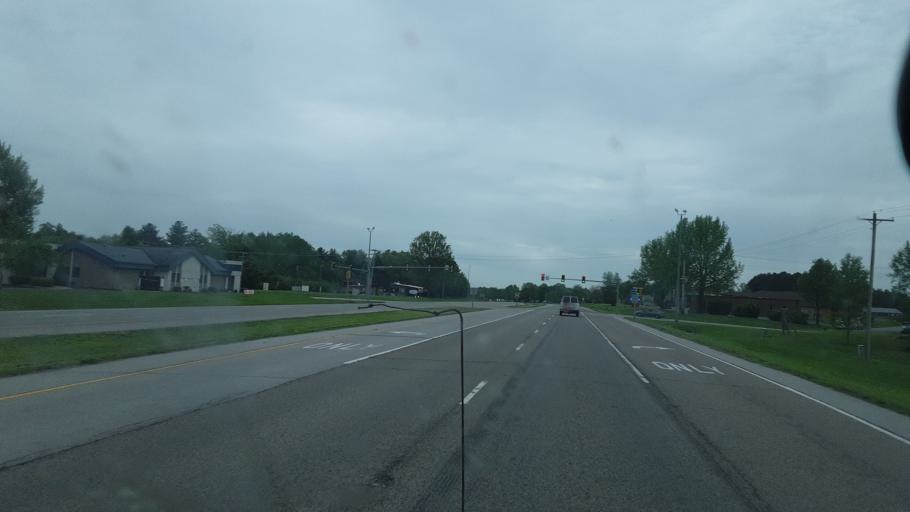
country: US
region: Illinois
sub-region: Jackson County
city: Carbondale
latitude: 37.7391
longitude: -89.2543
